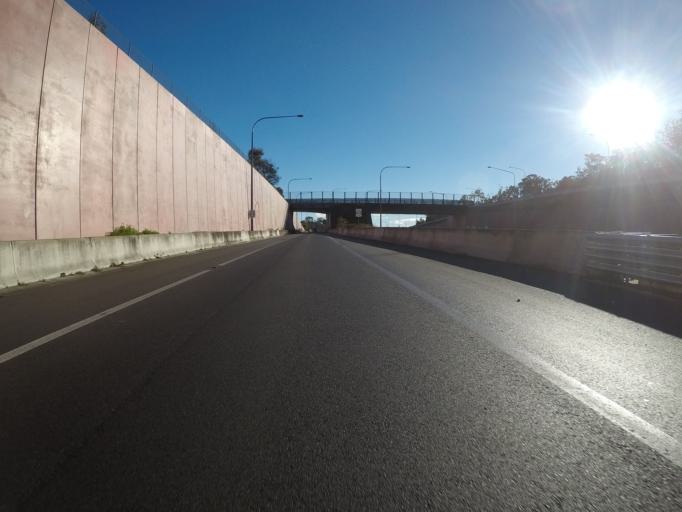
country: AU
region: Australian Capital Territory
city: Macquarie
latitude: -35.2623
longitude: 149.0863
